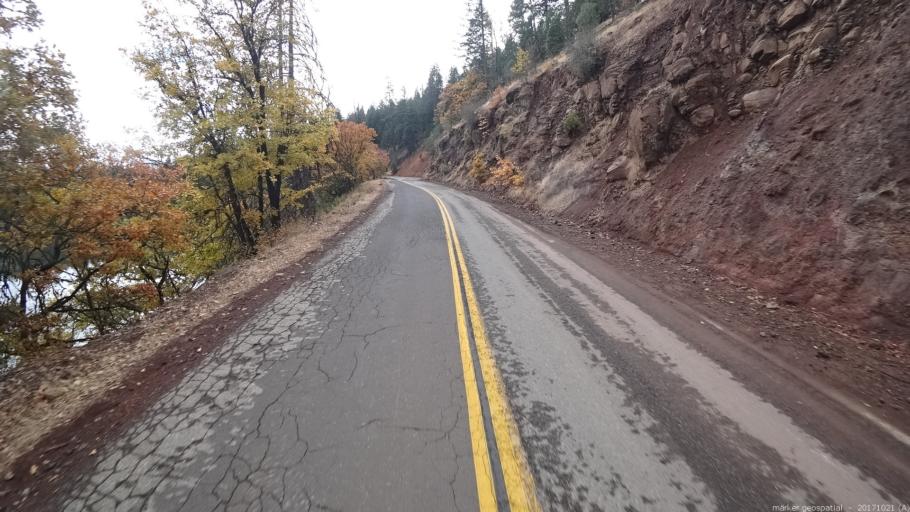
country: US
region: California
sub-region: Shasta County
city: Burney
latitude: 41.0215
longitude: -121.6720
